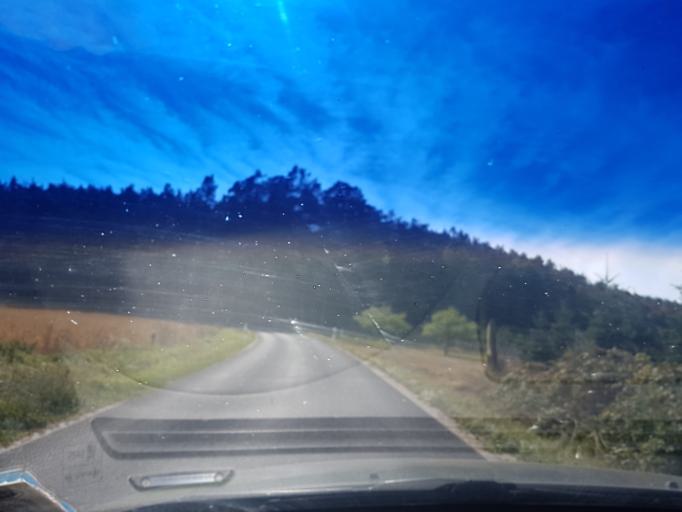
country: DE
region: Bavaria
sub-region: Regierungsbezirk Mittelfranken
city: Wachenroth
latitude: 49.7675
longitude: 10.7162
